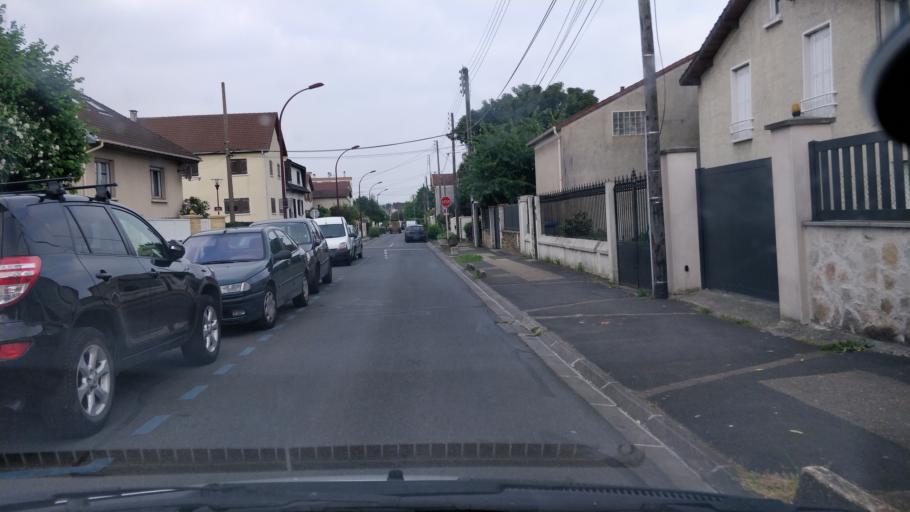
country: FR
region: Ile-de-France
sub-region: Departement de Seine-Saint-Denis
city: Bondy
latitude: 48.8907
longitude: 2.4815
